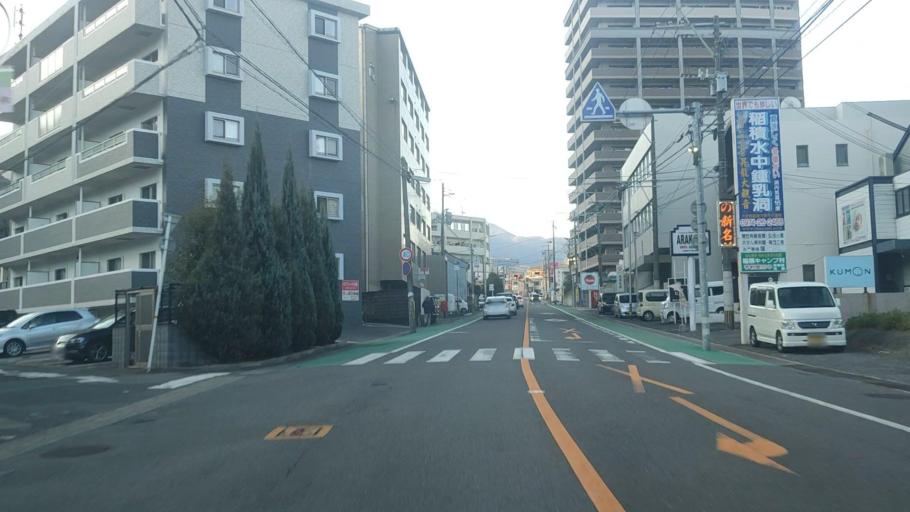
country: JP
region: Oita
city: Beppu
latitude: 33.2760
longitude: 131.4921
